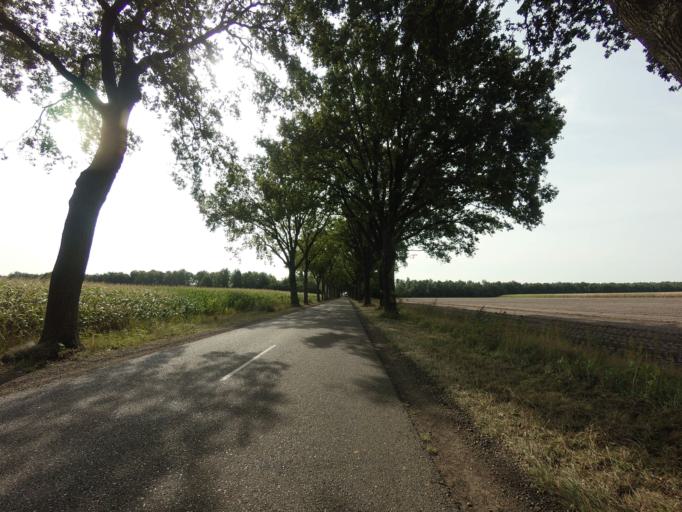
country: NL
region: North Brabant
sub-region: Gemeente Sint Anthonis
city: Sint Anthonis
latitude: 51.5997
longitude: 5.8359
